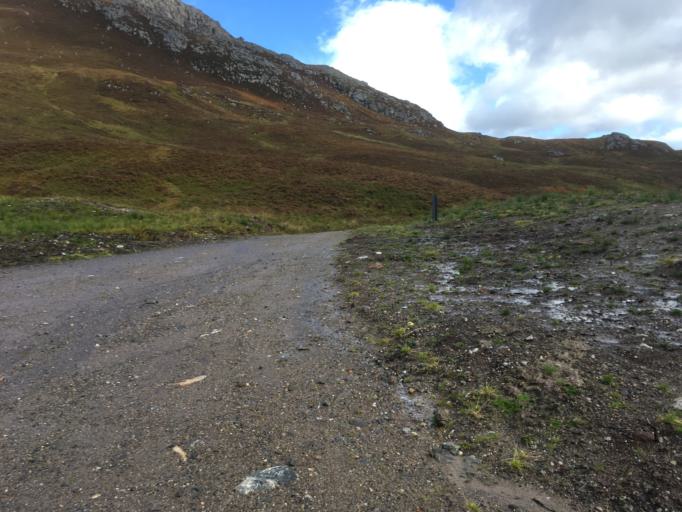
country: GB
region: Scotland
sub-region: Highland
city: Spean Bridge
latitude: 57.3416
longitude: -4.9813
